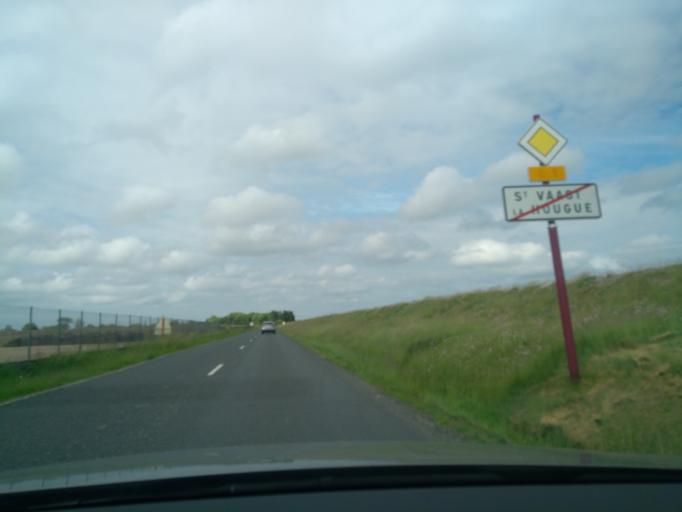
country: FR
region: Lower Normandy
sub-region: Departement de la Manche
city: Saint-Vaast-la-Hougue
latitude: 49.5968
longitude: -1.2644
